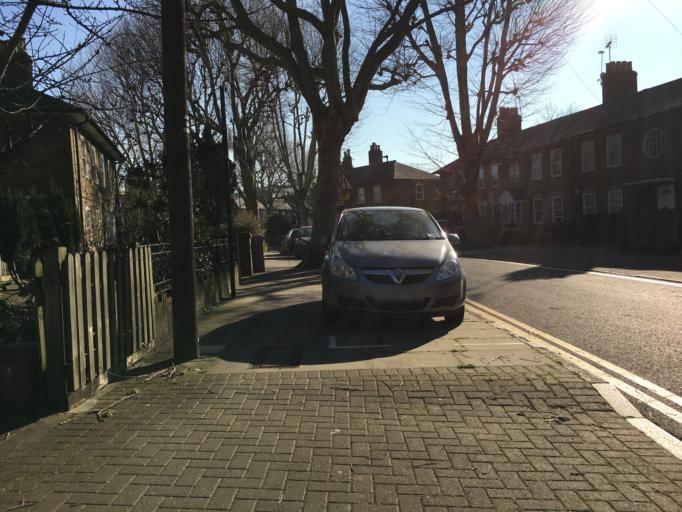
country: GB
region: England
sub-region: Greater London
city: Poplar
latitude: 51.4896
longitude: -0.0165
